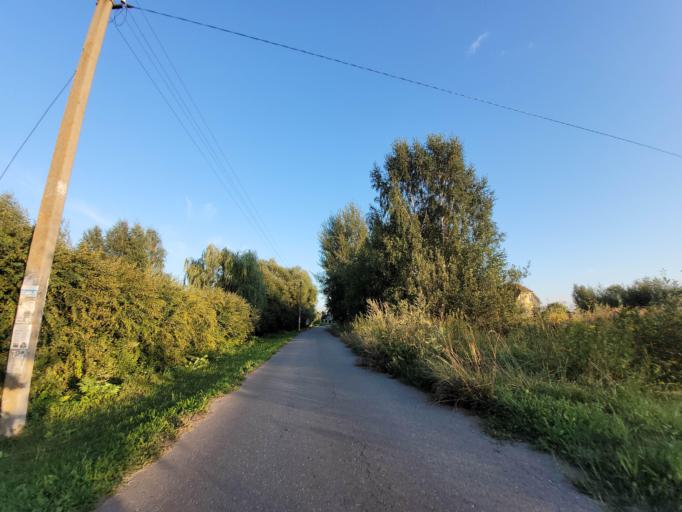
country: RU
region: Moskovskaya
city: Beloozerskiy
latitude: 55.4325
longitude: 38.4875
